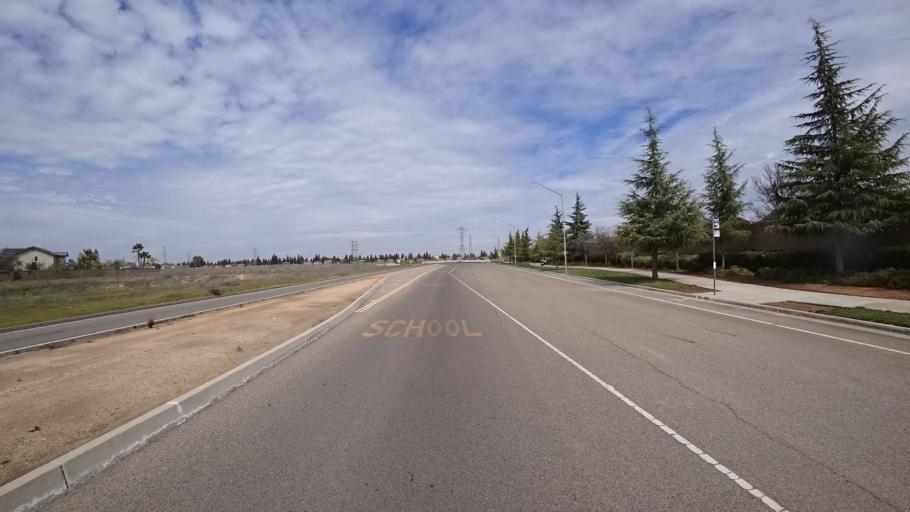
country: US
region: California
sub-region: Fresno County
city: Biola
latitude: 36.8322
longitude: -119.8990
